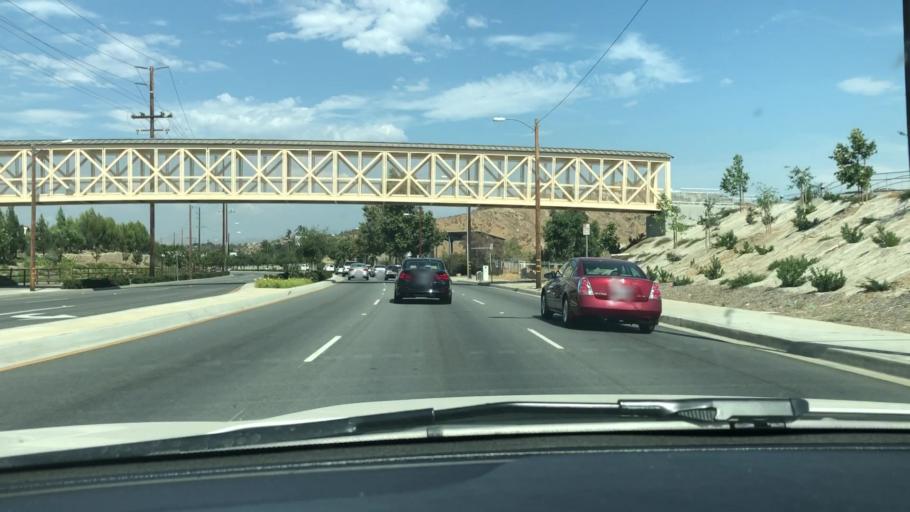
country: US
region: California
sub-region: Los Angeles County
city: Santa Clarita
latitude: 34.4145
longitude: -118.5231
